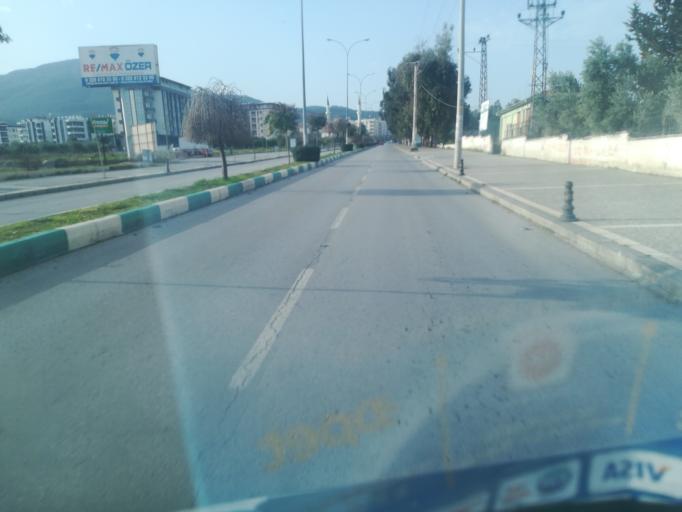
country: TR
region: Osmaniye
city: Osmaniye
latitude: 37.0481
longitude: 36.2271
